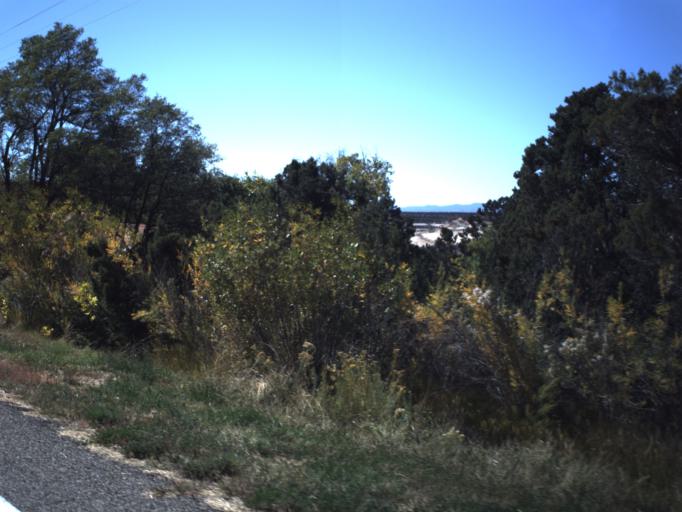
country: US
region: Utah
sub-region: Wayne County
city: Loa
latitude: 37.9085
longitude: -111.4243
